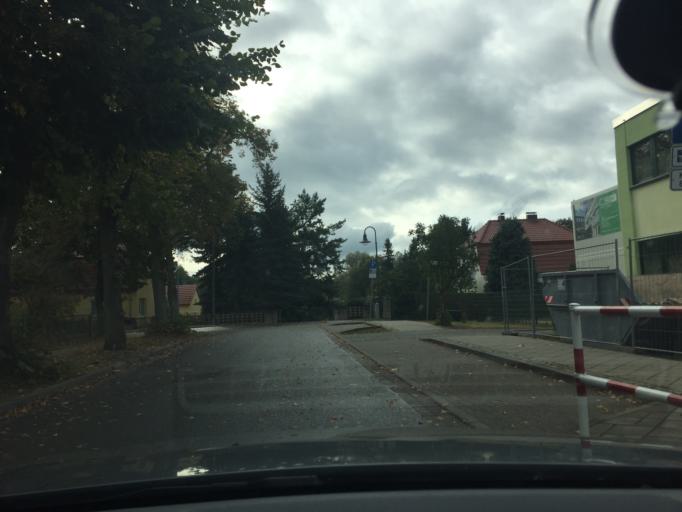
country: DE
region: Brandenburg
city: Erkner
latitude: 52.4194
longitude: 13.7519
